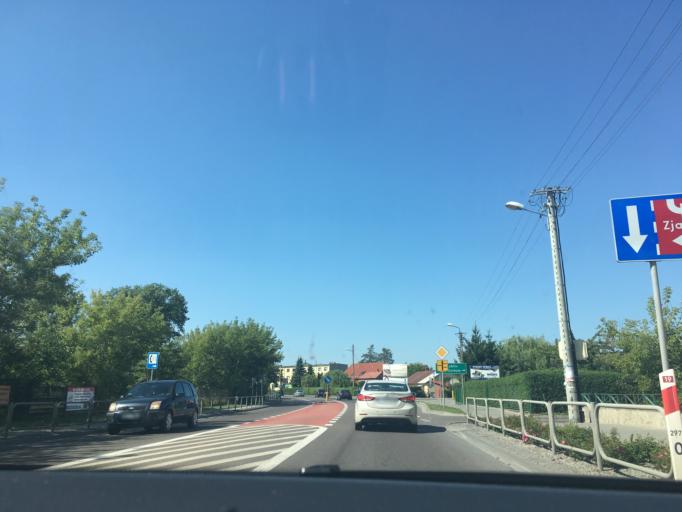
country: PL
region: Lublin Voivodeship
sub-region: Powiat lubelski
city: Niemce
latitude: 51.3588
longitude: 22.6237
